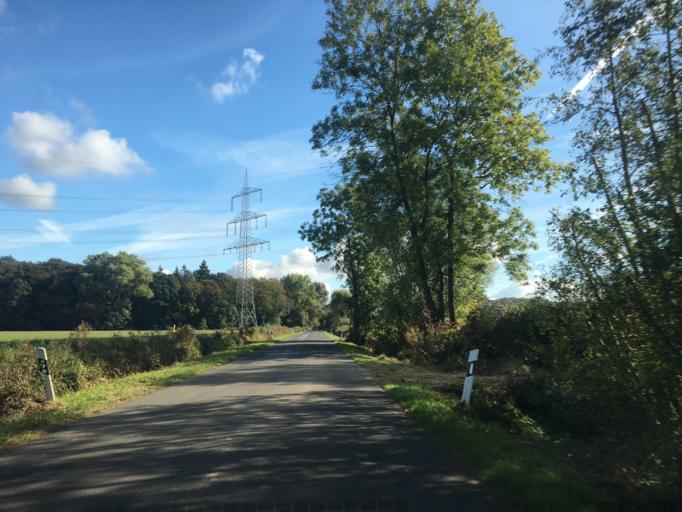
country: DE
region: North Rhine-Westphalia
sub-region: Regierungsbezirk Munster
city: Havixbeck
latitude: 51.9768
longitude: 7.4469
